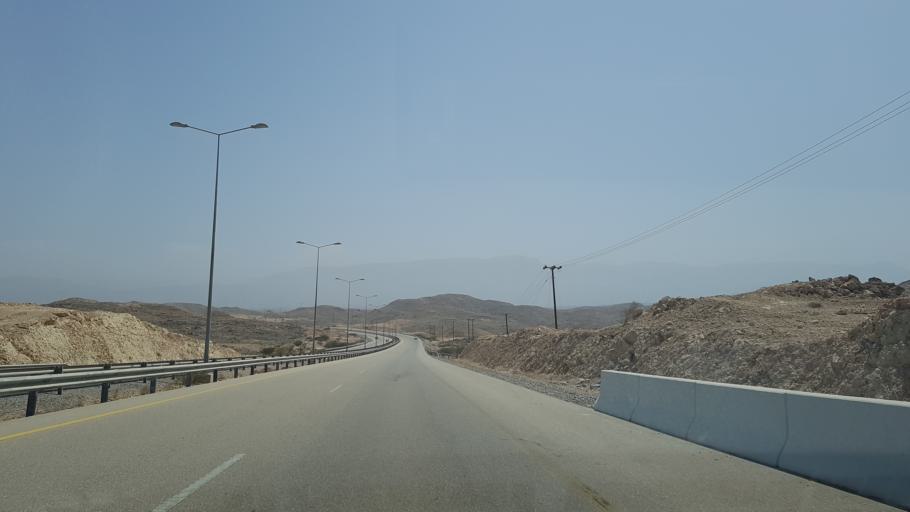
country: OM
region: Muhafazat Masqat
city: Muscat
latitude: 23.1689
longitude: 58.9767
